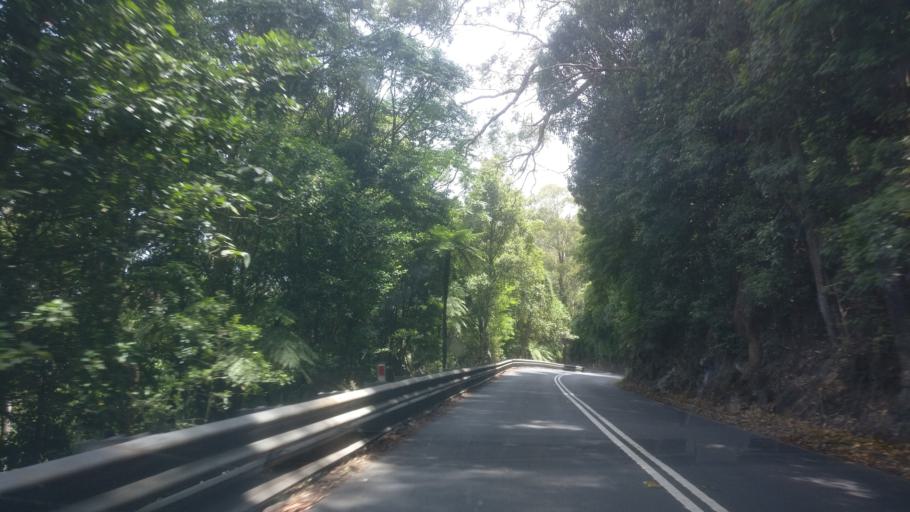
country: AU
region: New South Wales
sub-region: Shoalhaven Shire
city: Kangaroo Valley
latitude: -34.7900
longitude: 150.5637
